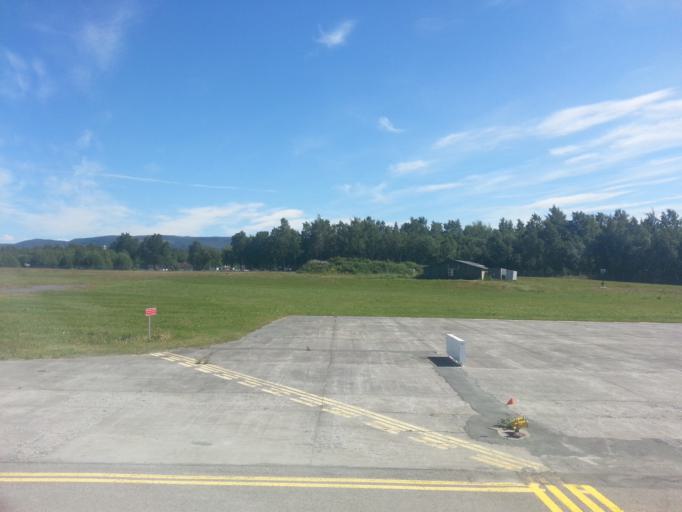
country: NO
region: Nord-Trondelag
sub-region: Stjordal
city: Stjordalshalsen
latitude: 63.4567
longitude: 10.9402
